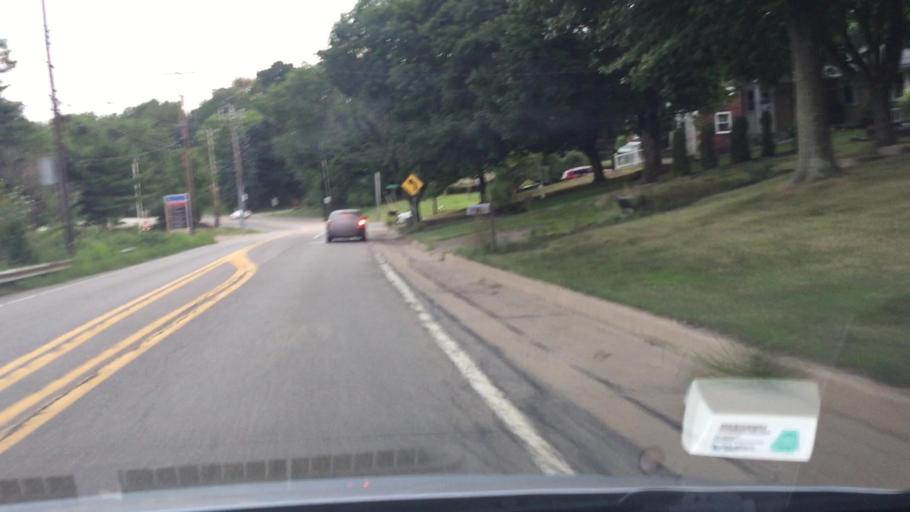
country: US
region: Pennsylvania
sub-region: Allegheny County
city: West View
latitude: 40.5750
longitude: -80.0160
